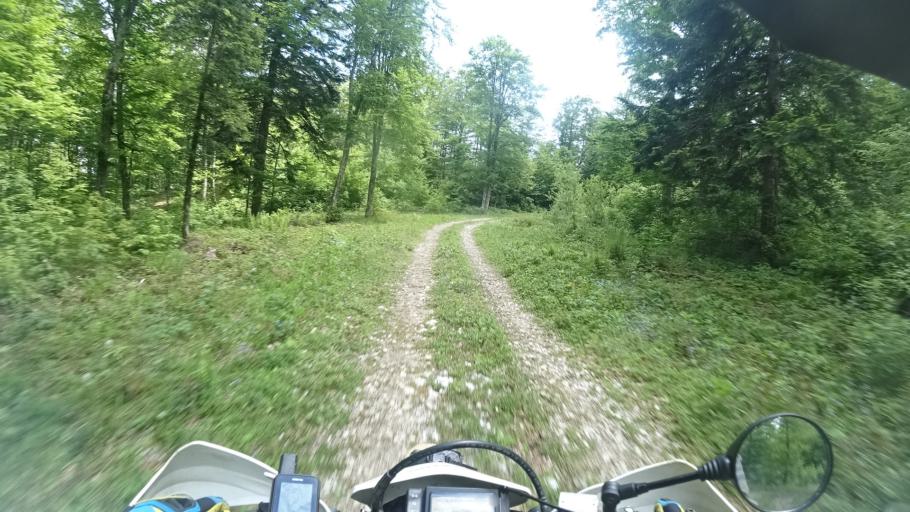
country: HR
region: Zadarska
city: Gracac
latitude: 44.4704
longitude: 15.8925
